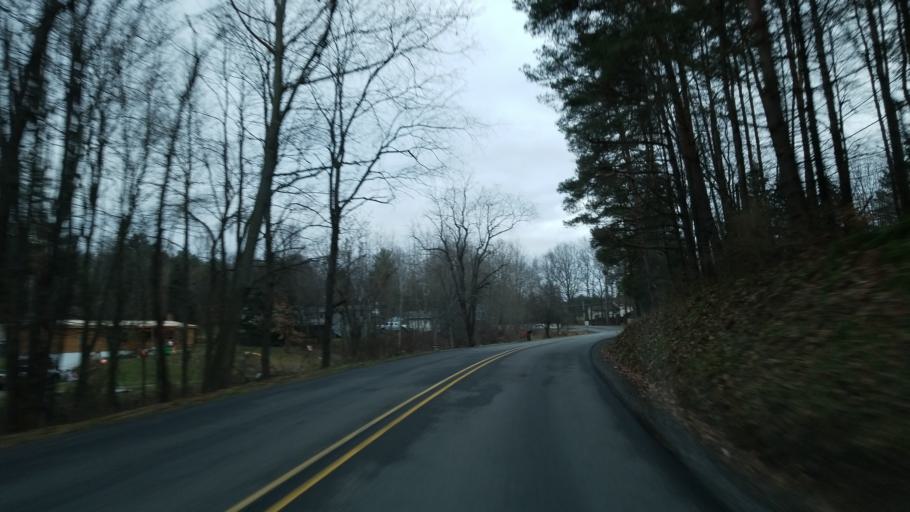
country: US
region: Pennsylvania
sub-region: Clearfield County
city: Sandy
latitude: 41.1163
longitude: -78.7902
